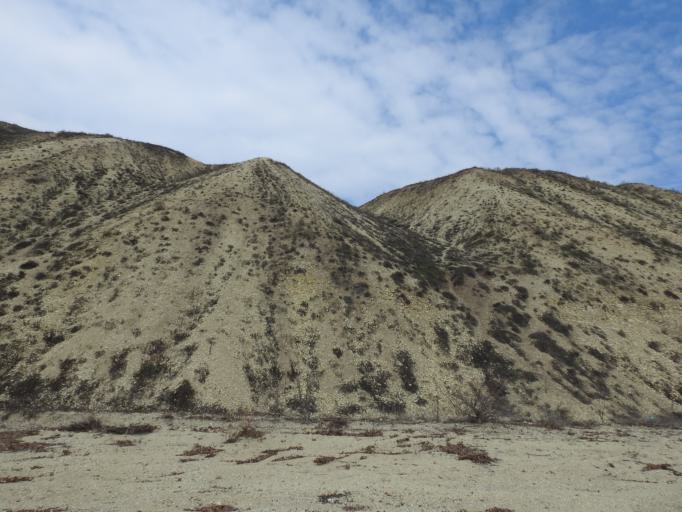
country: RU
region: Saratov
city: Voskresenskoye
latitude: 51.8063
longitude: 46.9162
